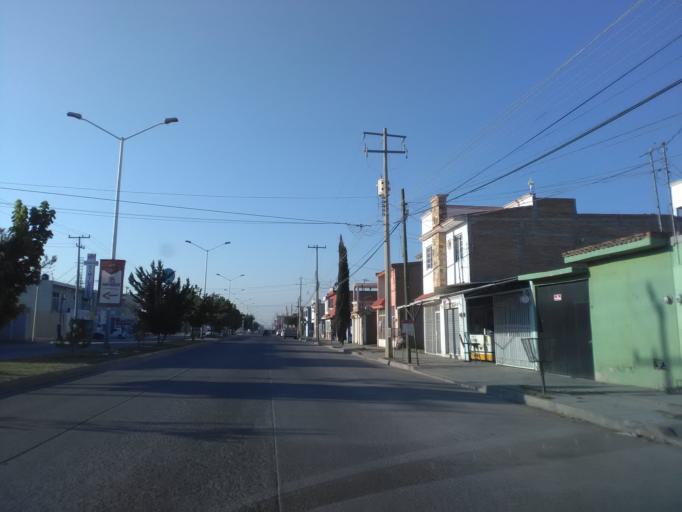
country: MX
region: Durango
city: Victoria de Durango
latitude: 24.0606
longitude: -104.6316
